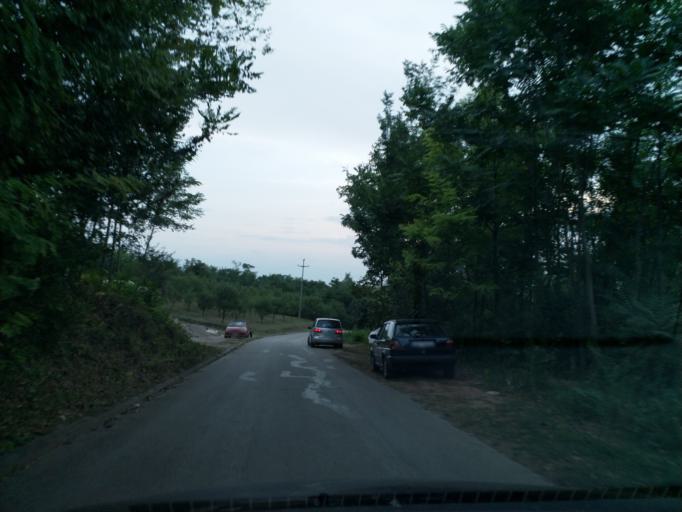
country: RS
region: Central Serbia
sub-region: Pomoravski Okrug
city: Paracin
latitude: 43.8498
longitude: 21.5341
